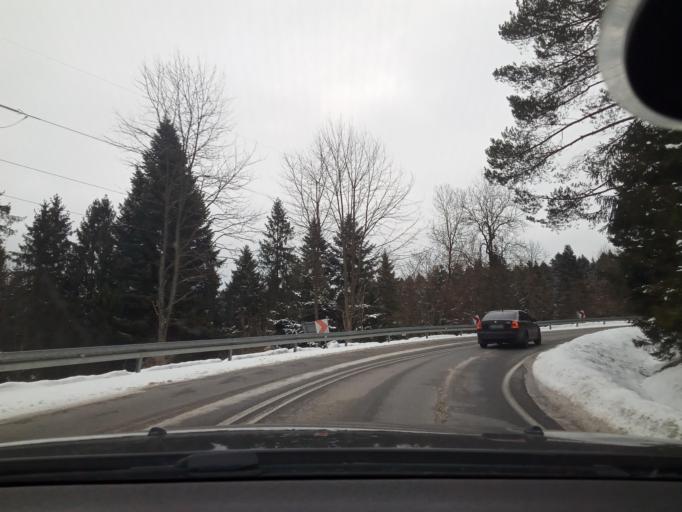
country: PL
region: Lesser Poland Voivodeship
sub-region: Powiat nowotarski
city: Krosnica
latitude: 49.4260
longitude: 20.3452
